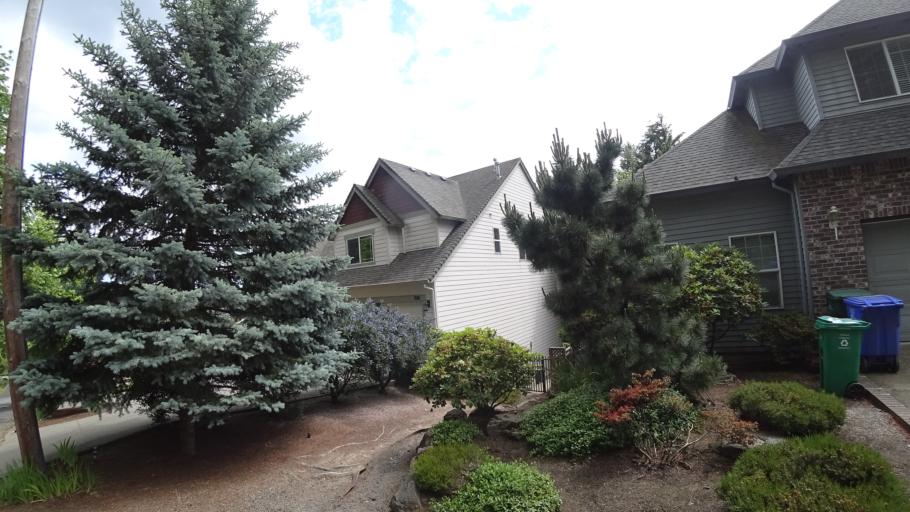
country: US
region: Oregon
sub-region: Clackamas County
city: Lake Oswego
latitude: 45.4473
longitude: -122.7091
